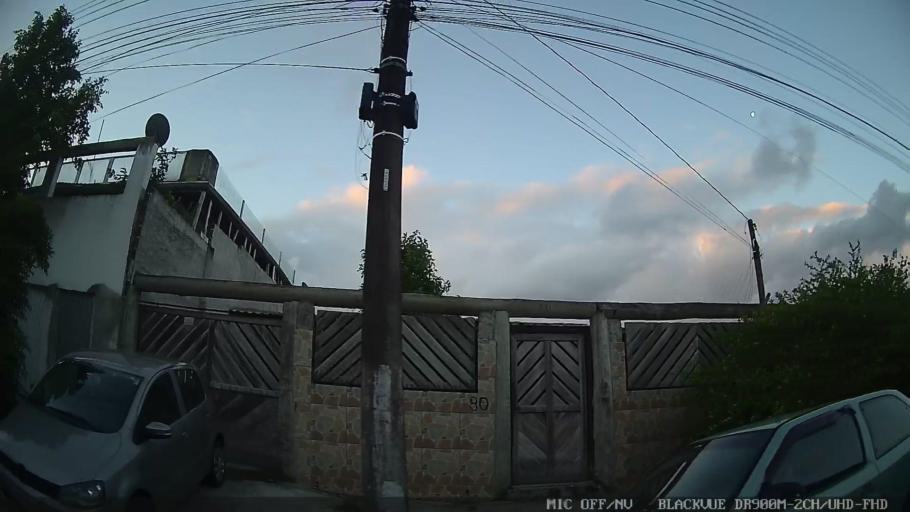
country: BR
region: Sao Paulo
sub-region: Caraguatatuba
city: Caraguatatuba
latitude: -23.6640
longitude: -45.4409
